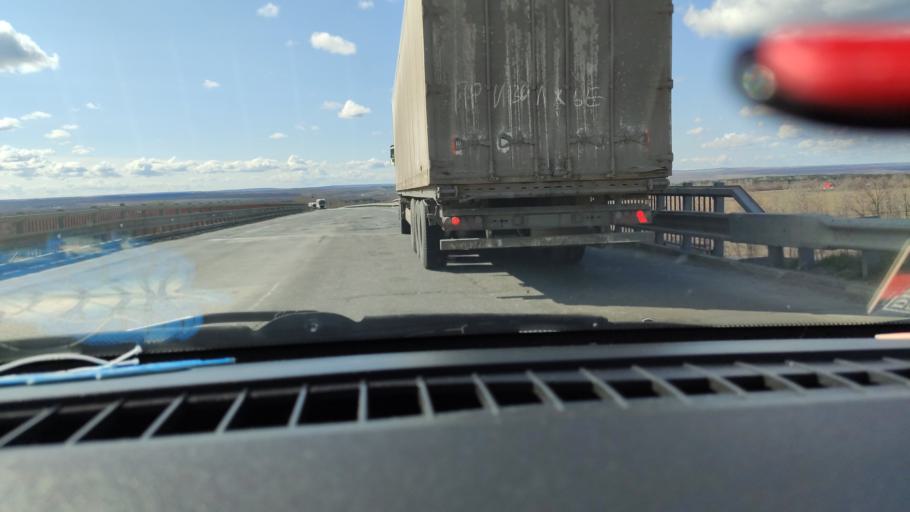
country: RU
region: Samara
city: Varlamovo
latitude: 53.1723
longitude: 48.2813
